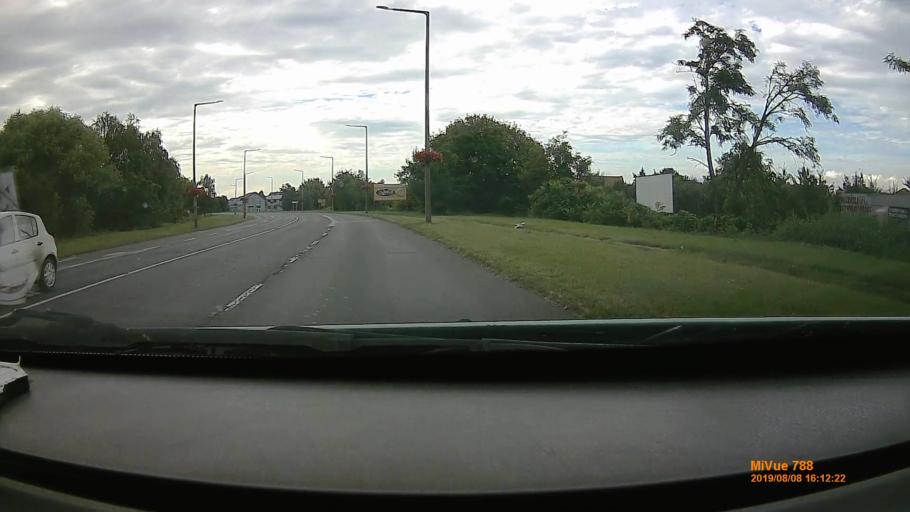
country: HU
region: Szabolcs-Szatmar-Bereg
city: Mateszalka
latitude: 47.9586
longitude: 22.3233
